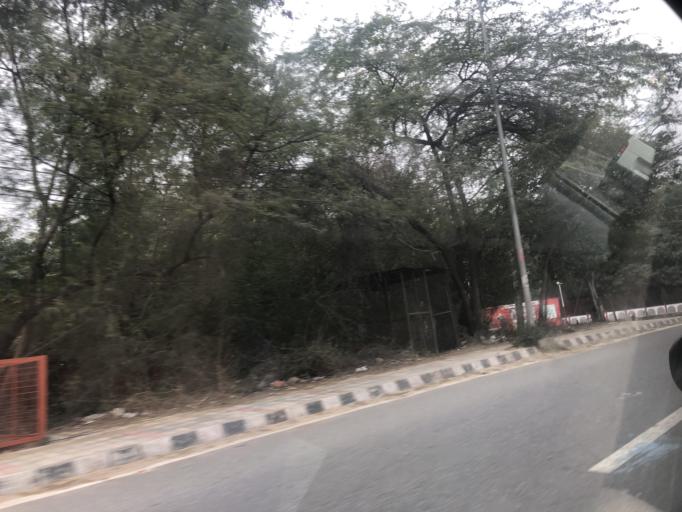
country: IN
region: NCT
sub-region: Central Delhi
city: Karol Bagh
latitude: 28.5741
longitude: 77.1531
